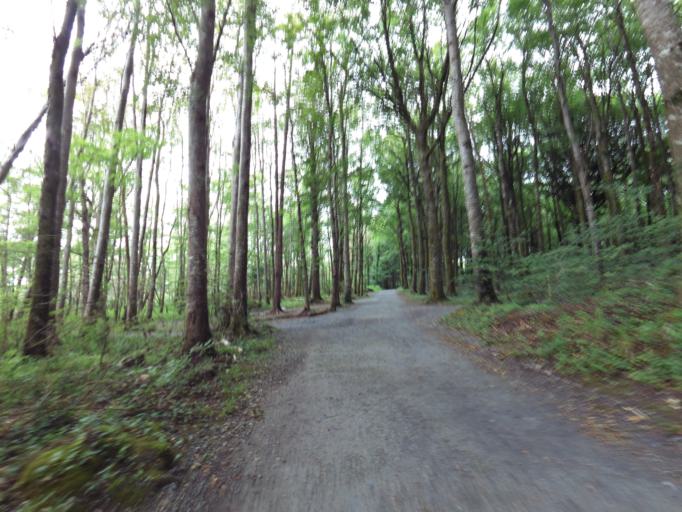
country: IE
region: Connaught
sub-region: County Galway
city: Gort
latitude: 53.0867
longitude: -8.8462
